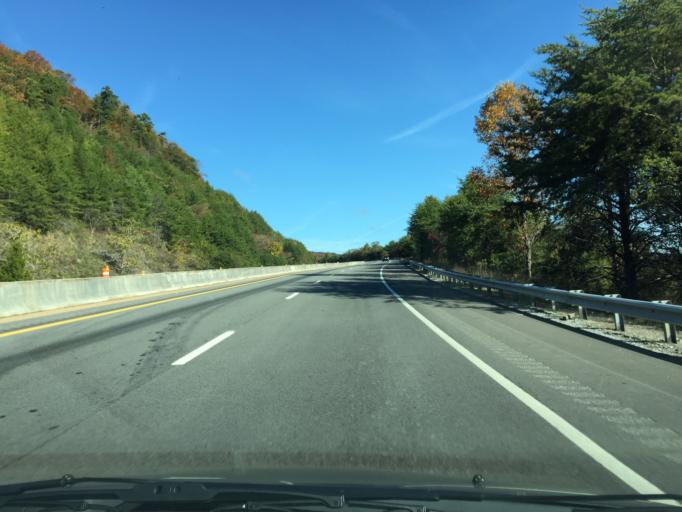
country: US
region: Tennessee
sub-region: Hamilton County
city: Sale Creek
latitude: 35.3165
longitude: -85.1615
